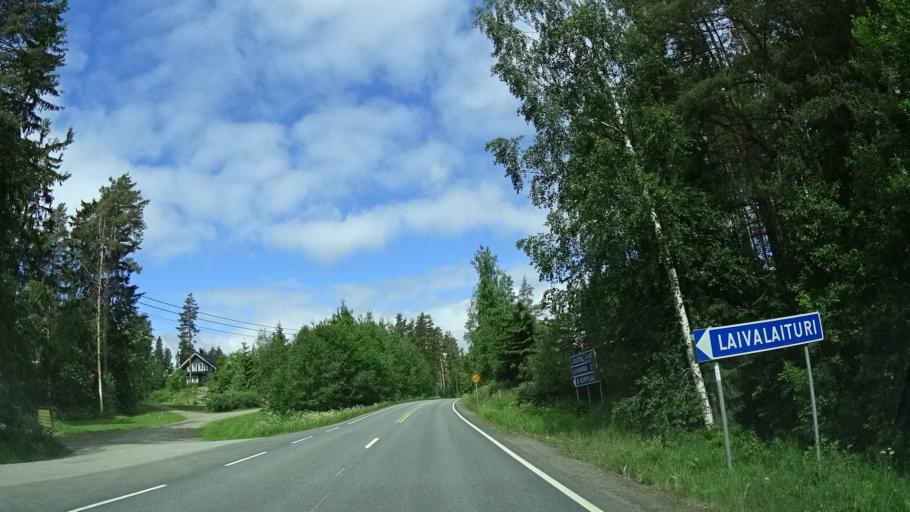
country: FI
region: Central Finland
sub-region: Jyvaeskylae
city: Korpilahti
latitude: 62.0082
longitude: 25.6606
